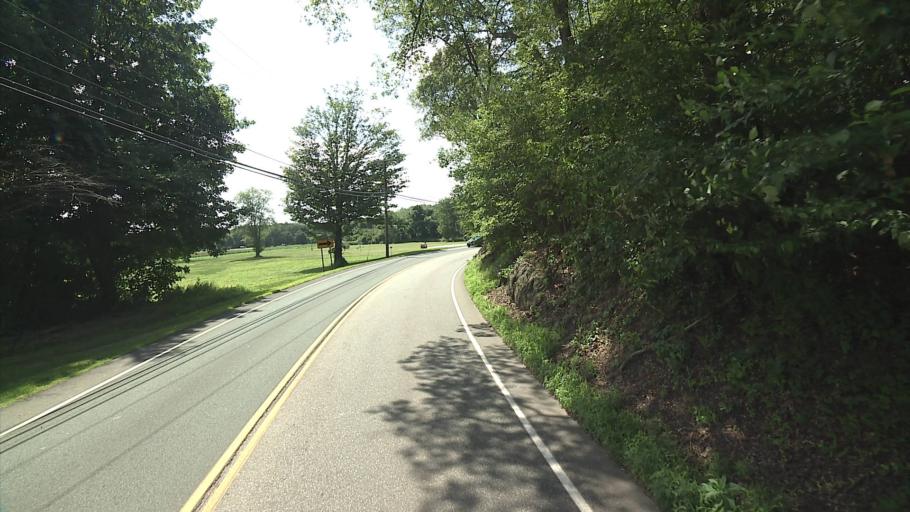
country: US
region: Connecticut
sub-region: Middlesex County
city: Essex Village
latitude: 41.3463
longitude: -72.4143
